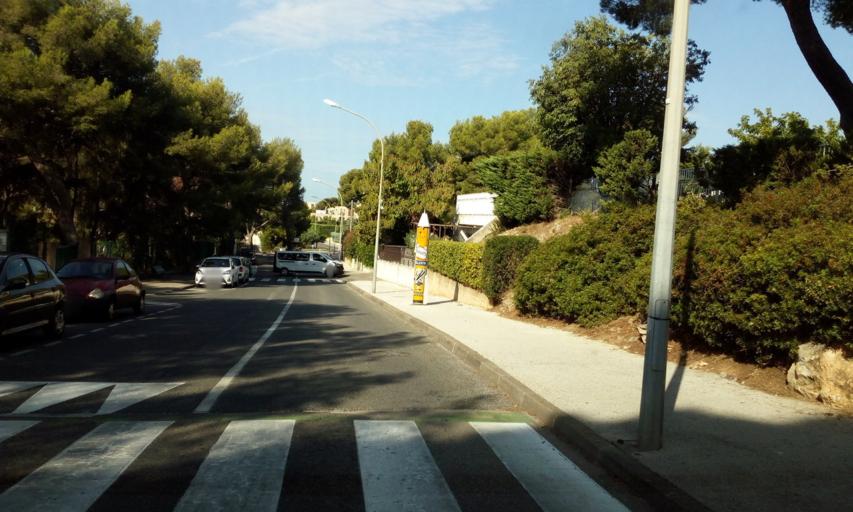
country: FR
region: Provence-Alpes-Cote d'Azur
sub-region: Departement du Var
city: Bandol
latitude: 43.1434
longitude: 5.7556
